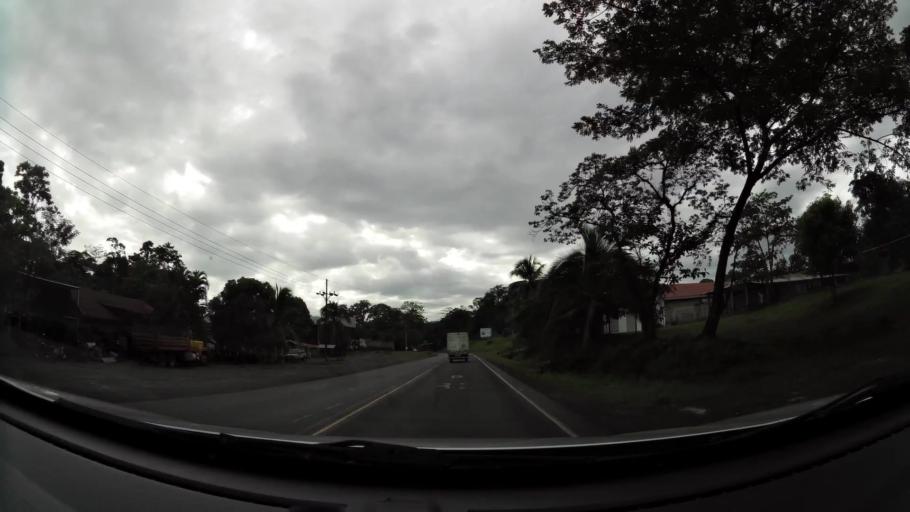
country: CR
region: Limon
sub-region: Canton de Siquirres
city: Siquirres
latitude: 10.1266
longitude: -83.5582
